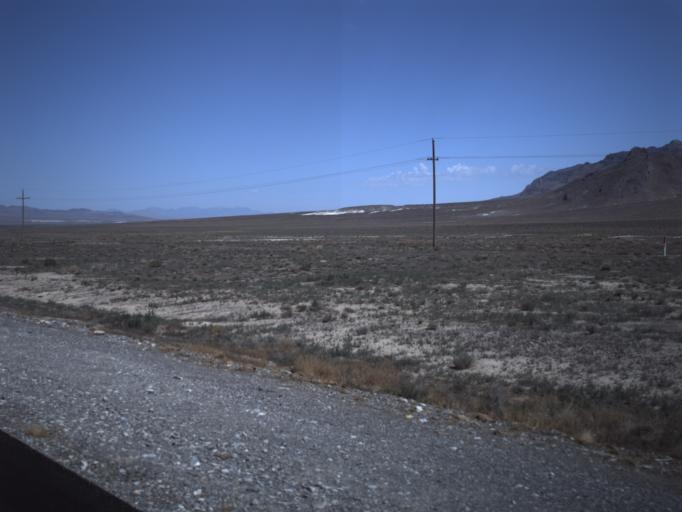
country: US
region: Utah
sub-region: Beaver County
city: Milford
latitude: 39.0558
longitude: -113.4293
